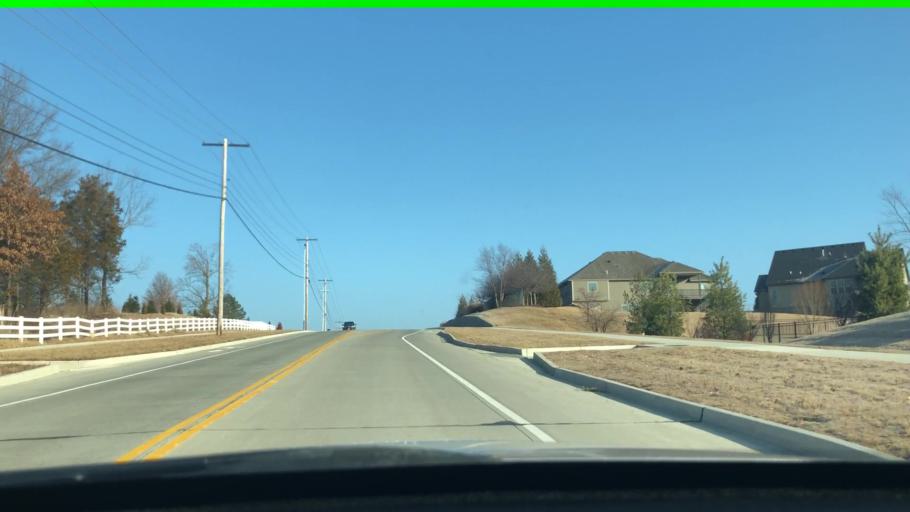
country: US
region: Missouri
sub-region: Boone County
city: Columbia
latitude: 38.9082
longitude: -92.4003
